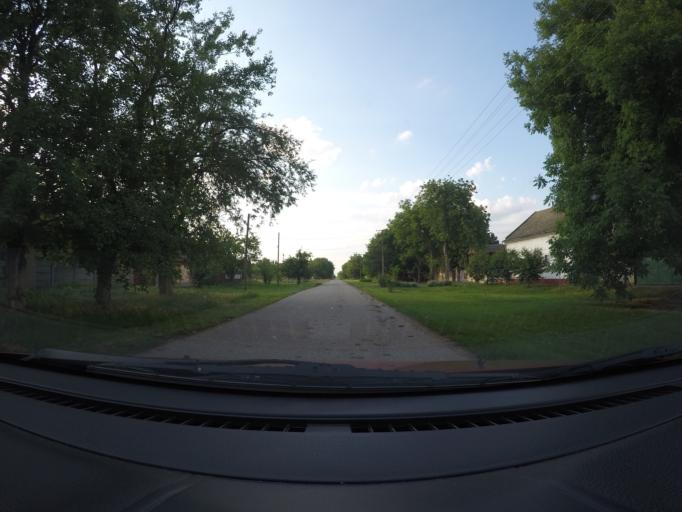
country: RS
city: Debeljaca
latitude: 45.0663
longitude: 20.6075
